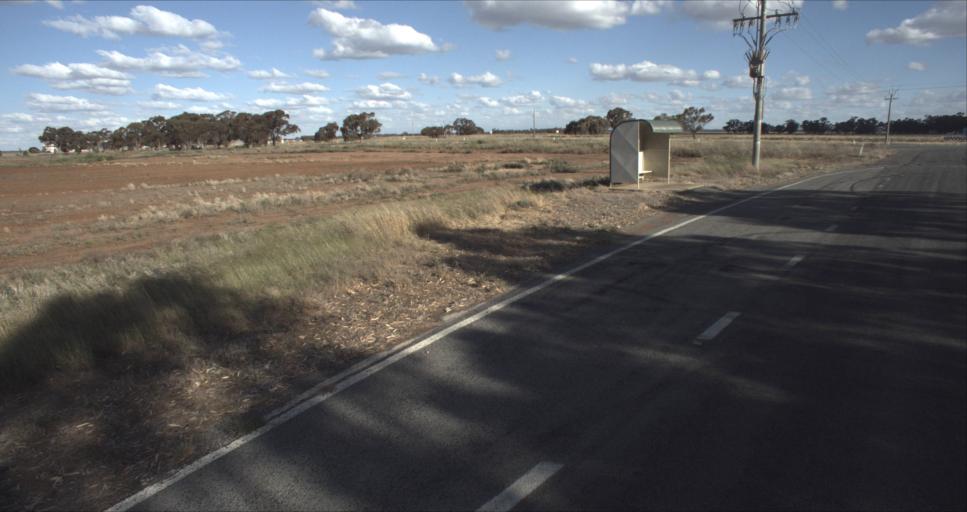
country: AU
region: New South Wales
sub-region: Leeton
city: Leeton
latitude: -34.5530
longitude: 146.2789
